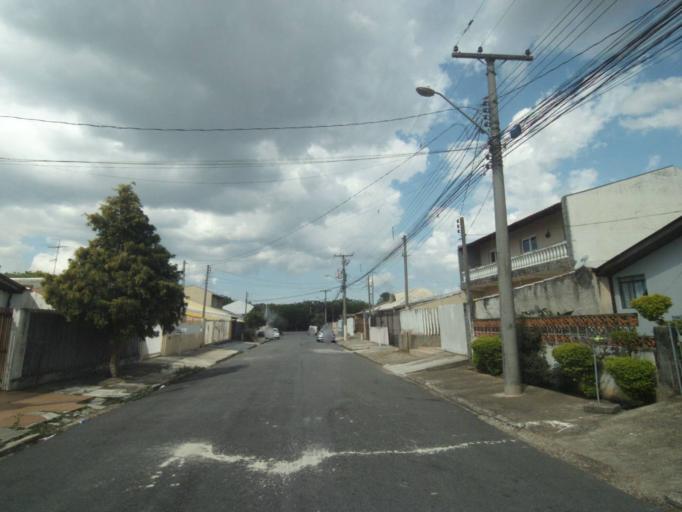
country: BR
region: Parana
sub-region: Sao Jose Dos Pinhais
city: Sao Jose dos Pinhais
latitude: -25.5286
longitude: -49.2631
